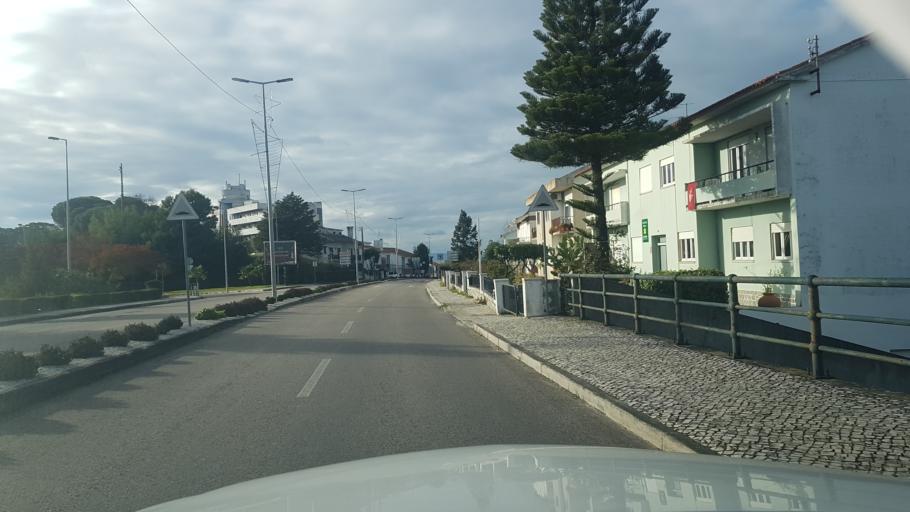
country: PT
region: Santarem
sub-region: Abrantes
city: Abrantes
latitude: 39.4633
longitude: -8.2097
